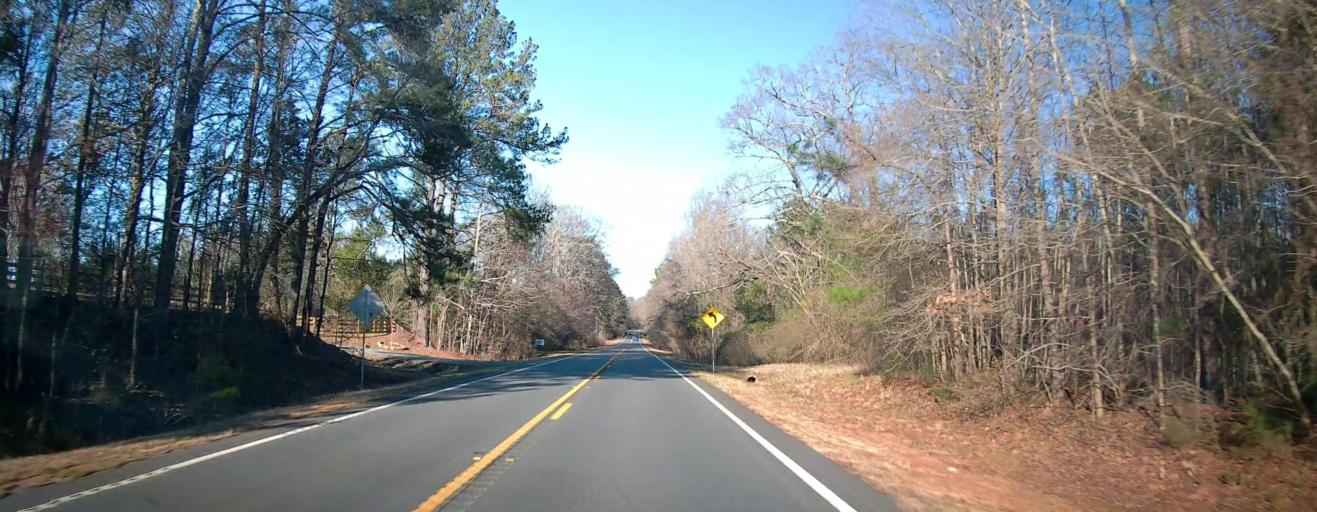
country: US
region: Georgia
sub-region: Meriwether County
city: Manchester
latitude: 32.9189
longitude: -84.6601
